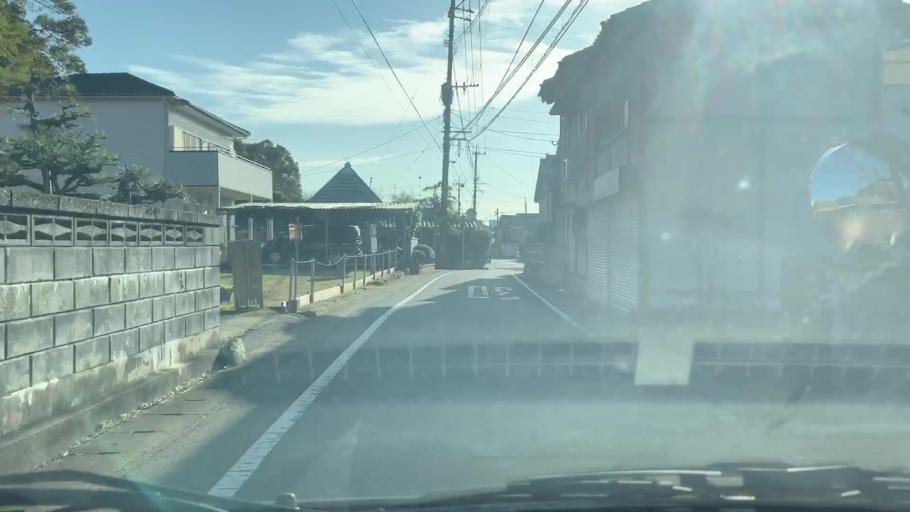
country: JP
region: Saga Prefecture
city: Takeocho-takeo
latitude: 33.2218
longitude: 130.0532
